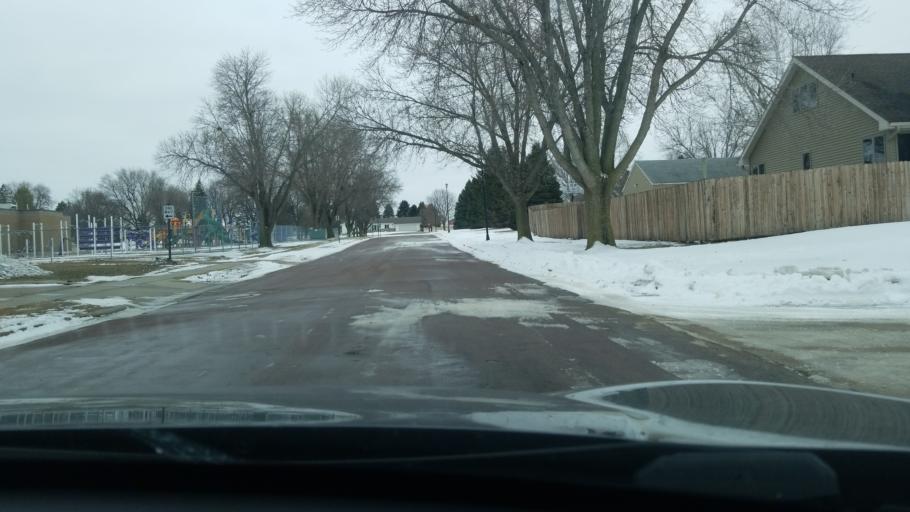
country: US
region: Iowa
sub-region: Lyon County
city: Rock Rapids
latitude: 43.4205
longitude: -96.1707
